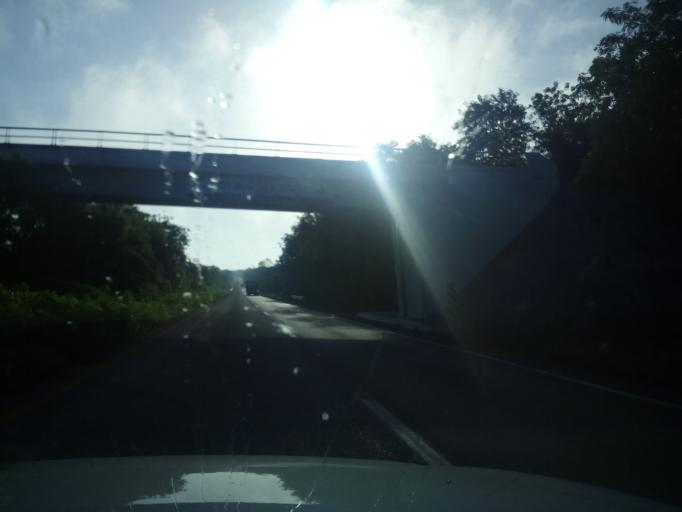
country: MX
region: Yucatan
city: Piste
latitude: 20.7462
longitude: -88.6978
